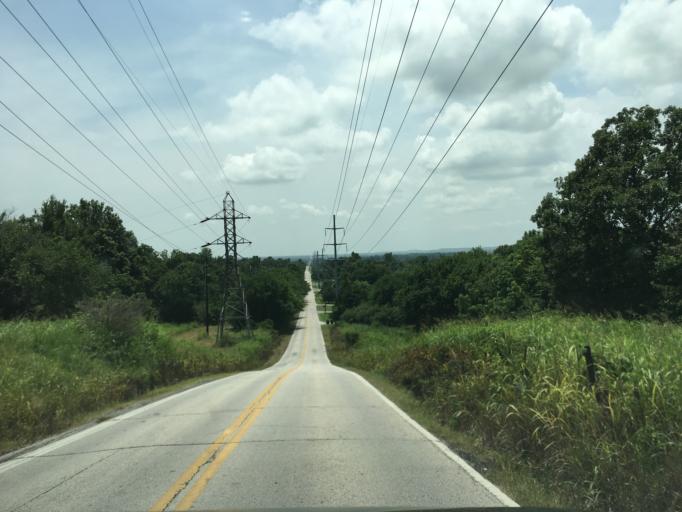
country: US
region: Oklahoma
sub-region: Tulsa County
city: Jenks
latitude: 36.0691
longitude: -95.9938
